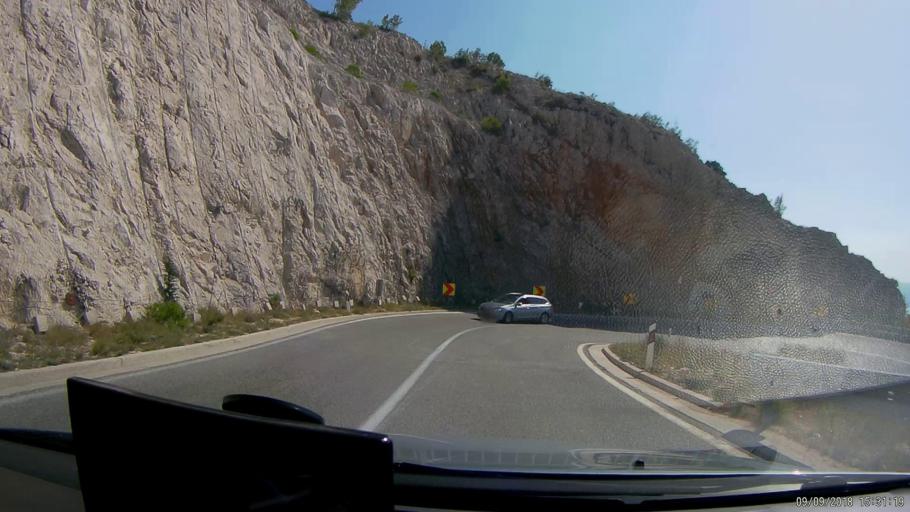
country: HR
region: Splitsko-Dalmatinska
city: Donja Brela
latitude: 43.3981
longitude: 16.8945
